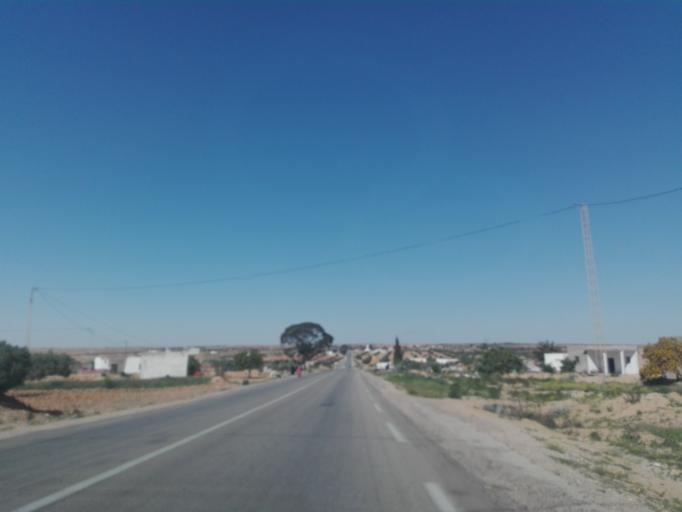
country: TN
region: Safaqis
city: Bi'r `Ali Bin Khalifah
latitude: 34.7410
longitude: 10.3844
